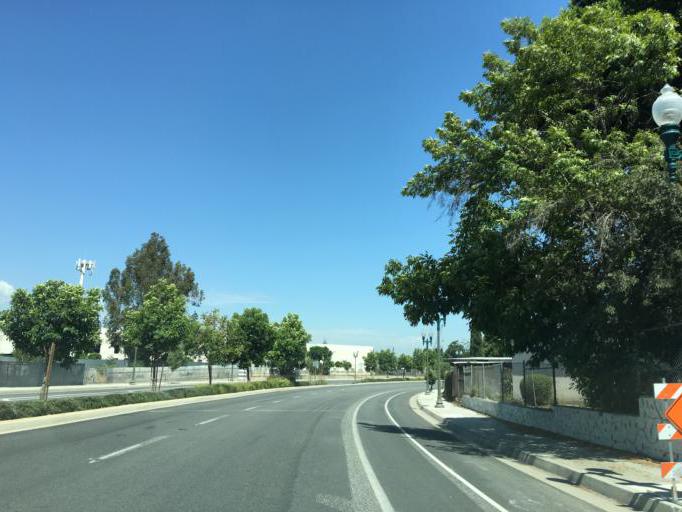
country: US
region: California
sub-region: Los Angeles County
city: Avocado Heights
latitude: 34.0438
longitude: -117.9949
